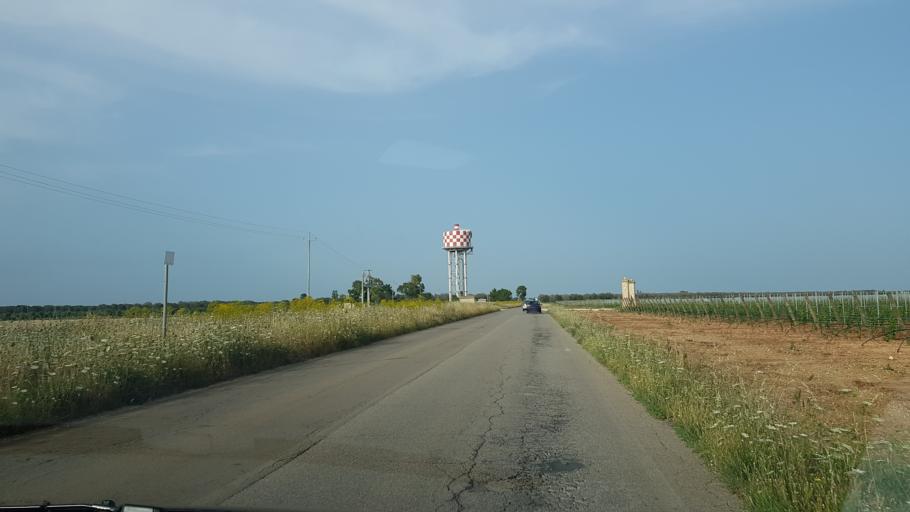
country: IT
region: Apulia
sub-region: Provincia di Brindisi
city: San Pancrazio Salentino
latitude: 40.4316
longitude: 17.8779
